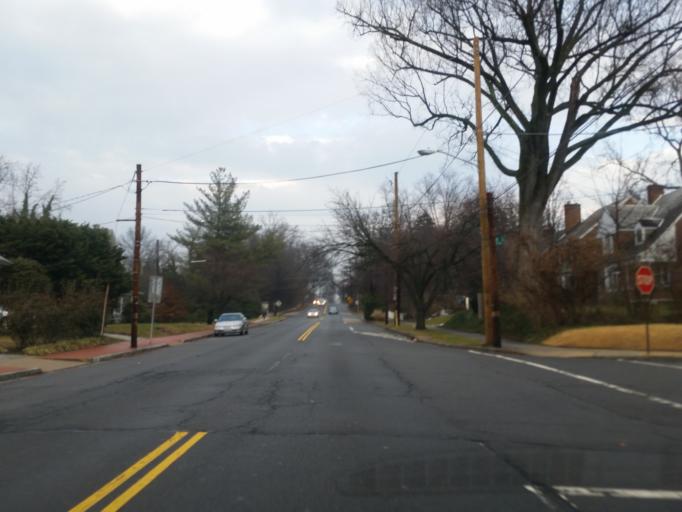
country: US
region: Maryland
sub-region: Montgomery County
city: Friendship Village
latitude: 38.9539
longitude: -77.0946
